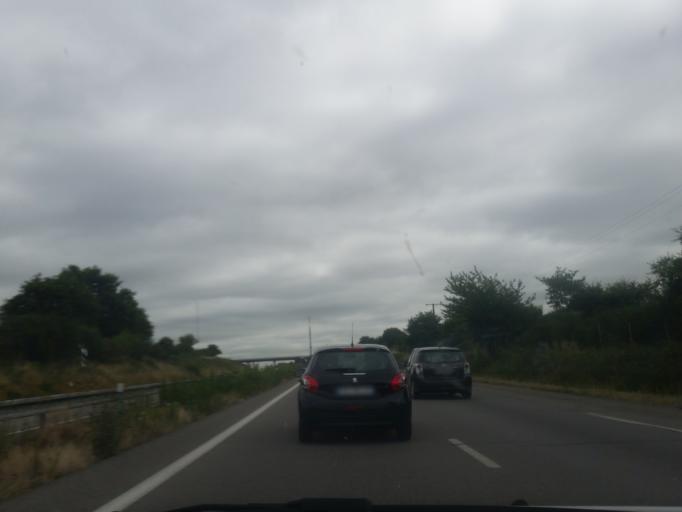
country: FR
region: Pays de la Loire
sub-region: Departement de la Loire-Atlantique
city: Thouare-sur-Loire
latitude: 47.2972
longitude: -1.4403
